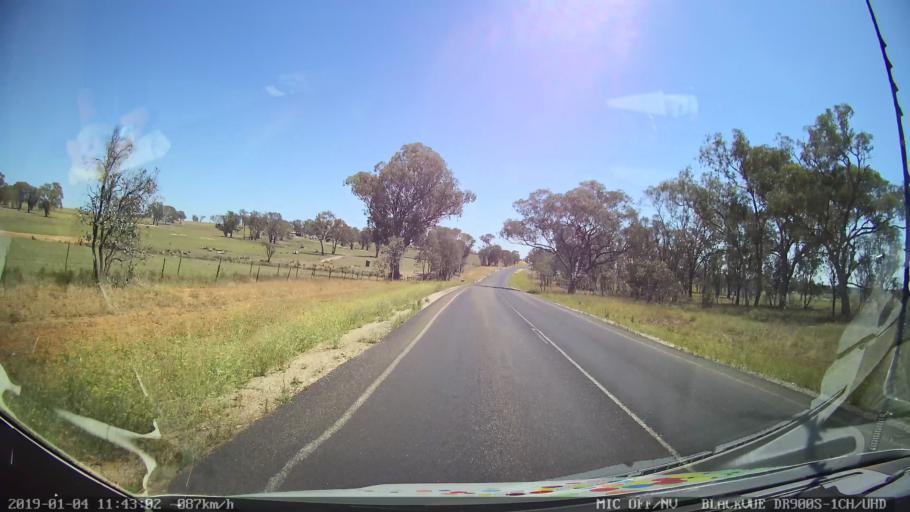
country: AU
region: New South Wales
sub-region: Cabonne
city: Molong
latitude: -32.9742
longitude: 148.7847
